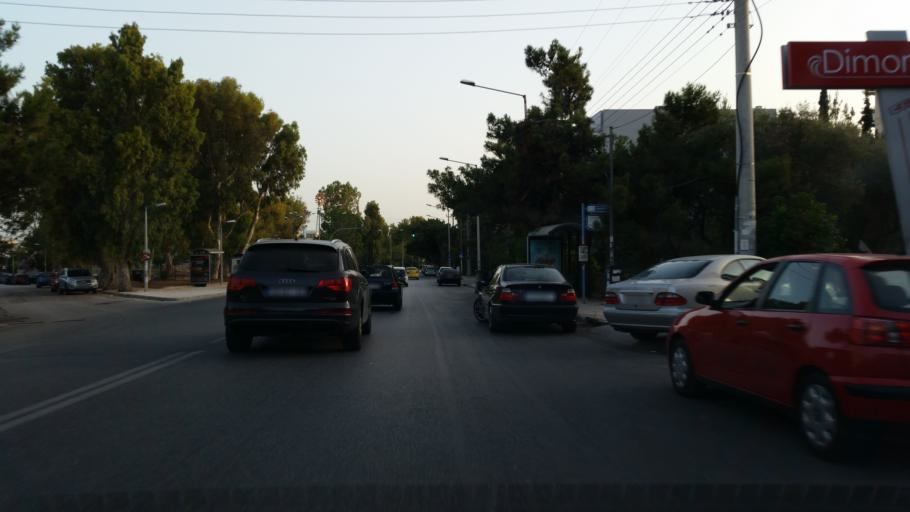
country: GR
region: Attica
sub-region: Nomarchia Athinas
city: Glyfada
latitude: 37.8657
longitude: 23.7557
